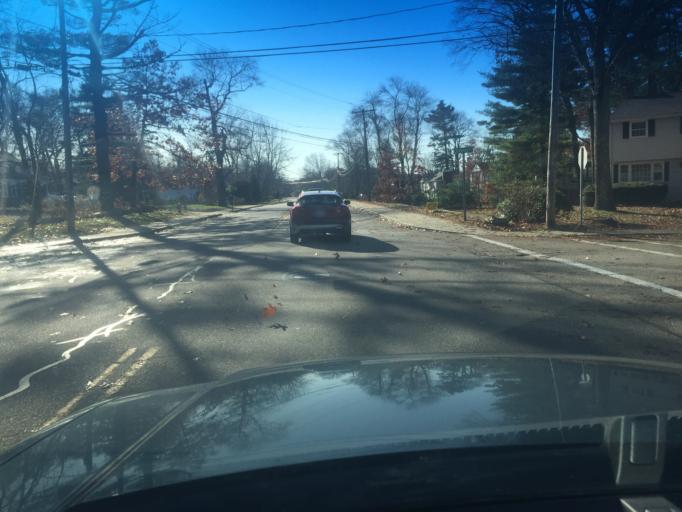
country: US
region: Massachusetts
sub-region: Norfolk County
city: Franklin
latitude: 42.1023
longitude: -71.4282
